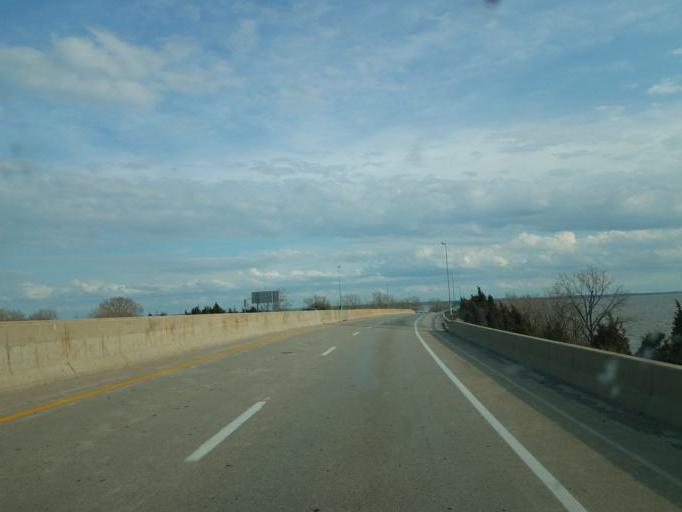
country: US
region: Ohio
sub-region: Ottawa County
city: Port Clinton
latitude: 41.5003
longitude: -82.8371
